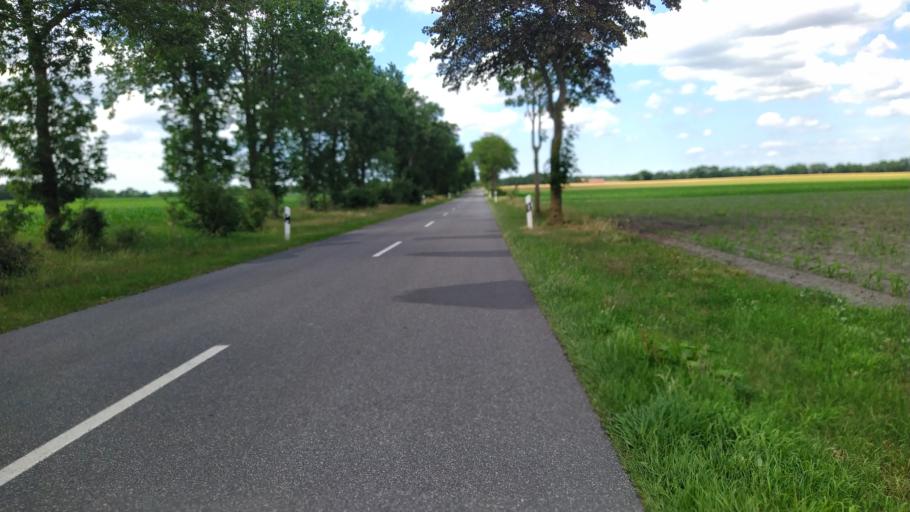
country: DE
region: Lower Saxony
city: Hollnseth
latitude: 53.5771
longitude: 9.1120
